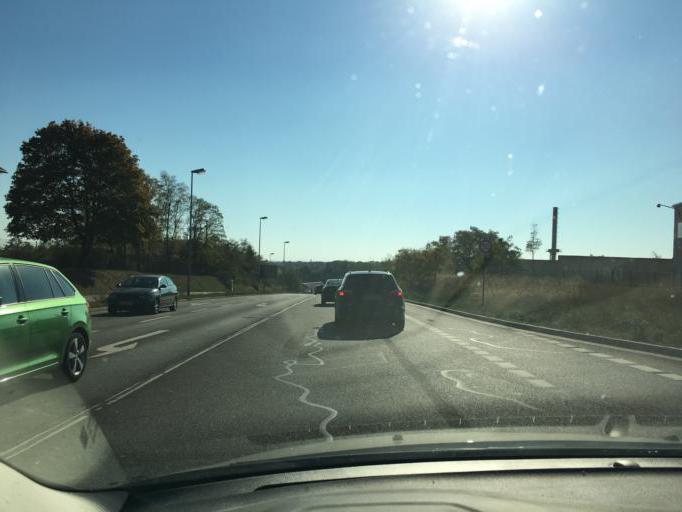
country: DE
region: Saxony-Anhalt
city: Bernburg
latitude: 51.8084
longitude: 11.7252
